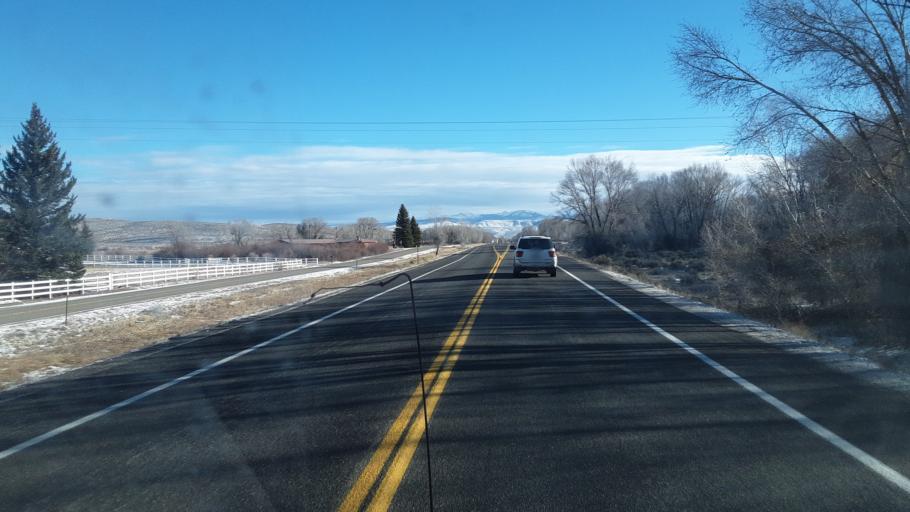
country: US
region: Colorado
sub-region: Gunnison County
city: Gunnison
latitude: 38.5244
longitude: -106.9718
